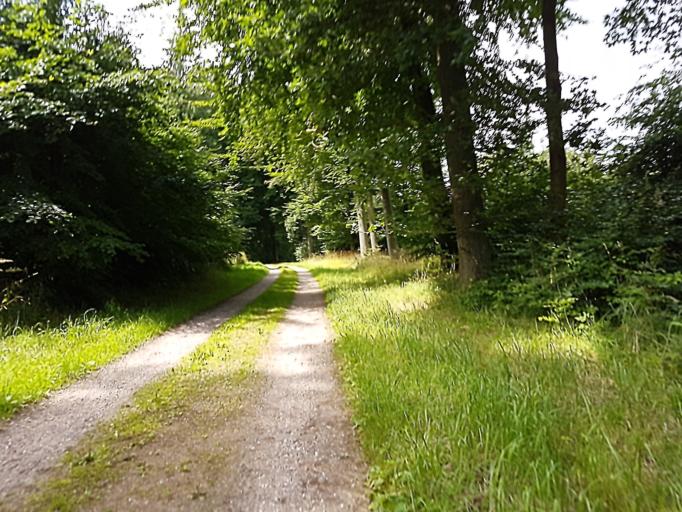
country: DK
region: Capital Region
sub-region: Fureso Kommune
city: Farum
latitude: 55.7969
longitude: 12.3508
